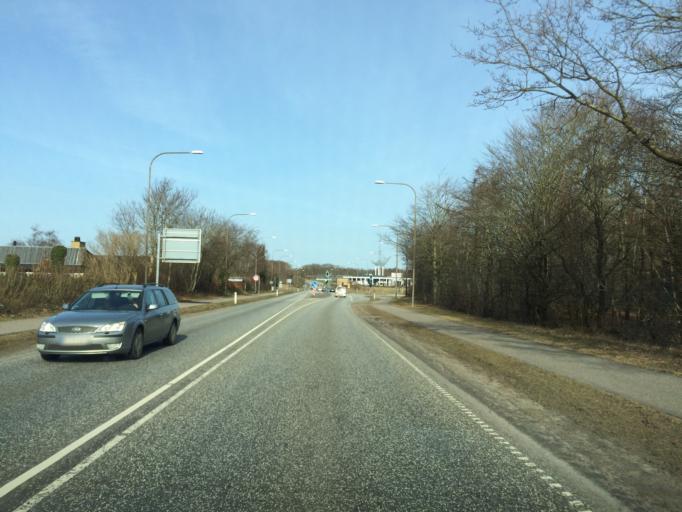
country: DK
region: Central Jutland
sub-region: Holstebro Kommune
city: Holstebro
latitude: 56.3480
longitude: 8.6346
